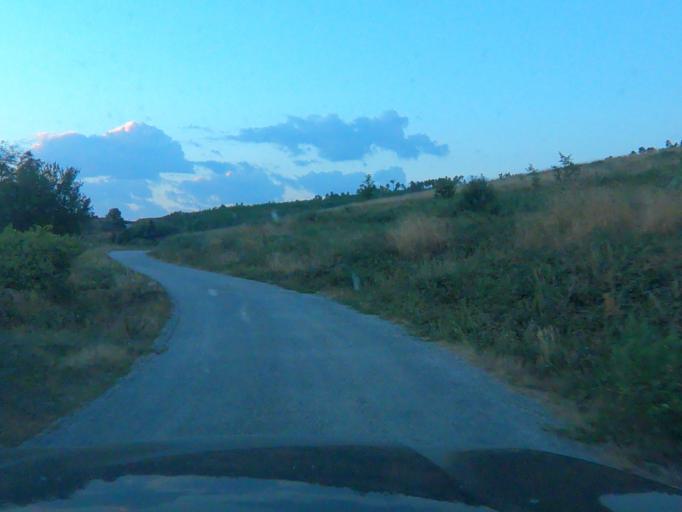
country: PT
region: Vila Real
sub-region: Sabrosa
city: Sabrosa
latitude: 41.2695
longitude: -7.6221
